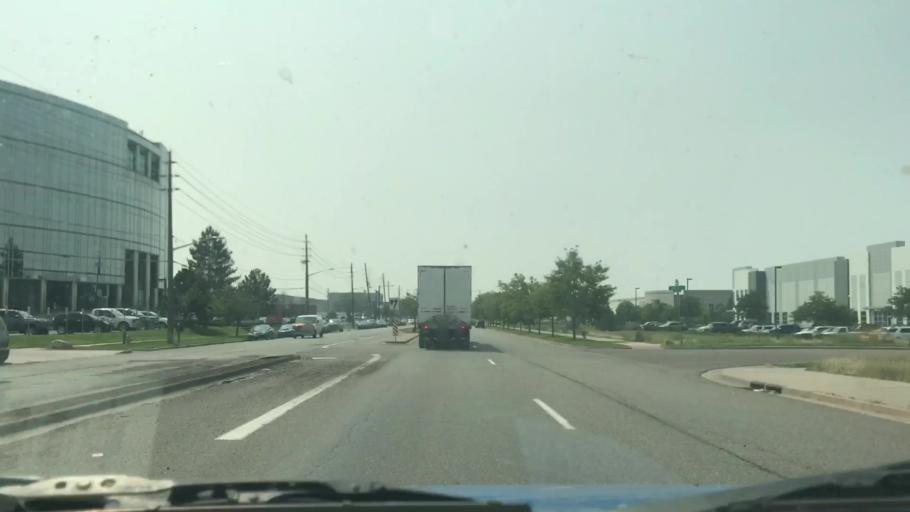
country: US
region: Colorado
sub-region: Adams County
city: Aurora
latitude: 39.7852
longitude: -104.8659
